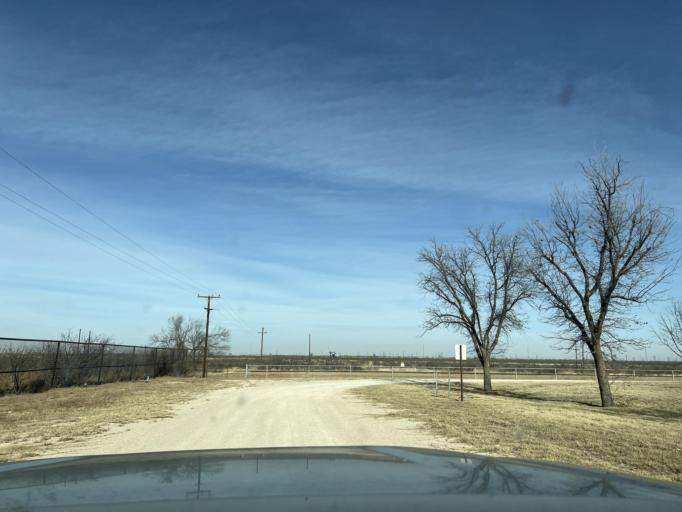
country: US
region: Texas
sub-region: Andrews County
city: Andrews
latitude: 32.4561
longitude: -102.5714
